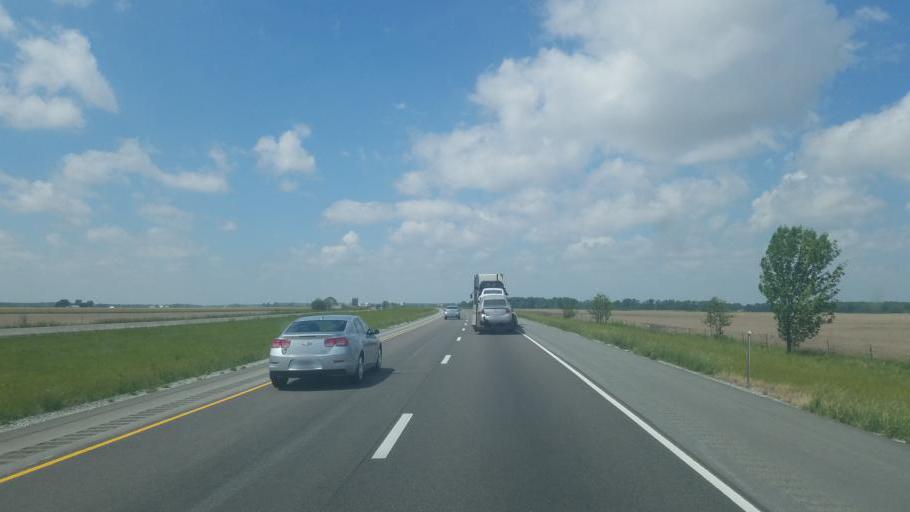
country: US
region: Illinois
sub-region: Clark County
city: Casey
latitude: 39.3156
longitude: -88.0022
